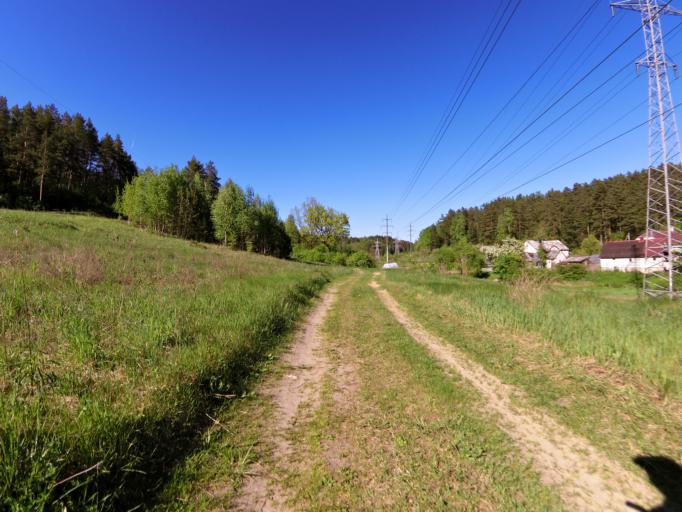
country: LT
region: Vilnius County
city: Pilaite
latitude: 54.6782
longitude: 25.1728
